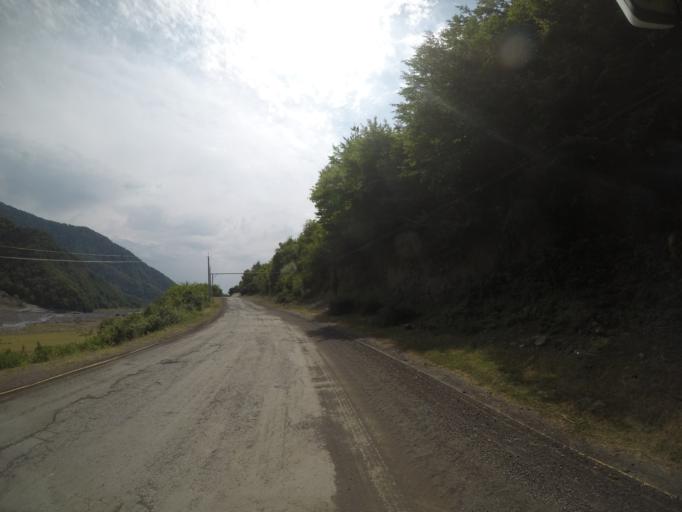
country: AZ
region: Qakh Rayon
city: Qaxbas
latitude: 41.4573
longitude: 47.0202
